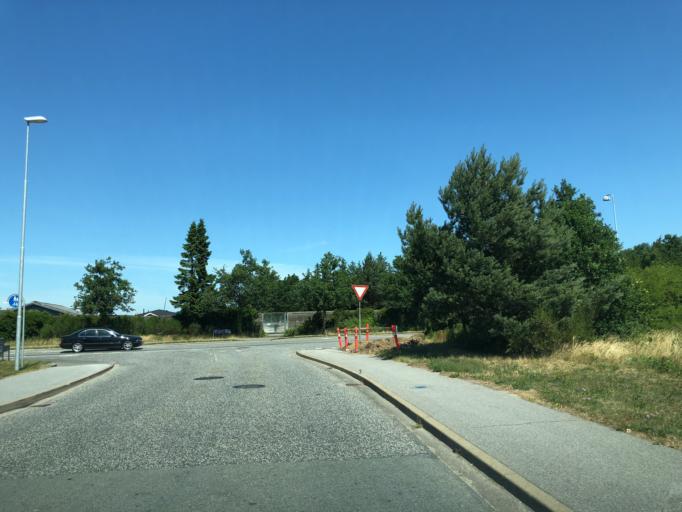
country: DK
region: Central Jutland
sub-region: Skive Kommune
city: Skive
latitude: 56.5427
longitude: 9.0296
